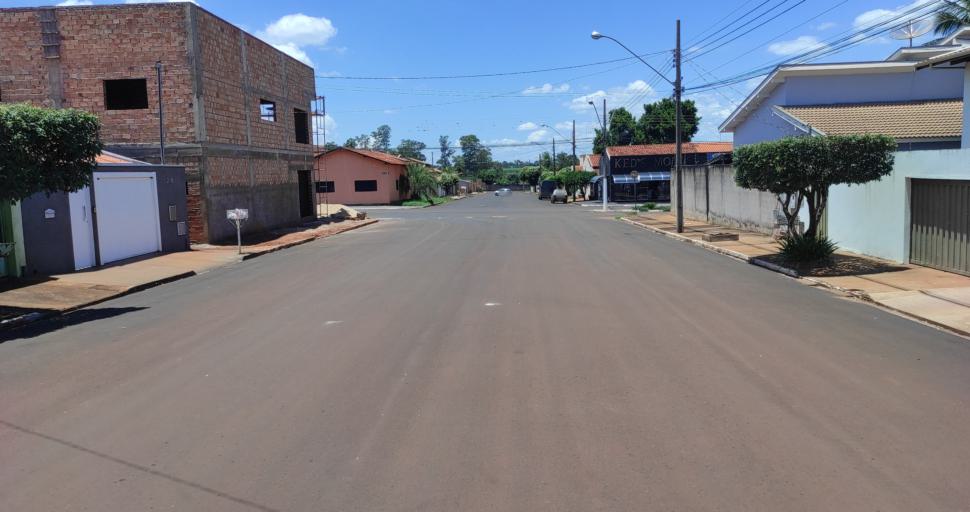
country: BR
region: Minas Gerais
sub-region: Frutal
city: Frutal
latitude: -20.1418
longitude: -48.7015
